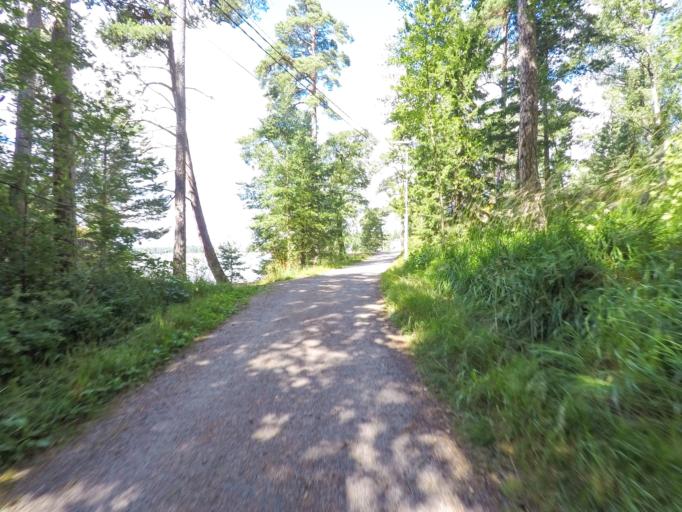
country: FI
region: Uusimaa
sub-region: Helsinki
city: Helsinki
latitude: 60.1772
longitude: 25.0221
